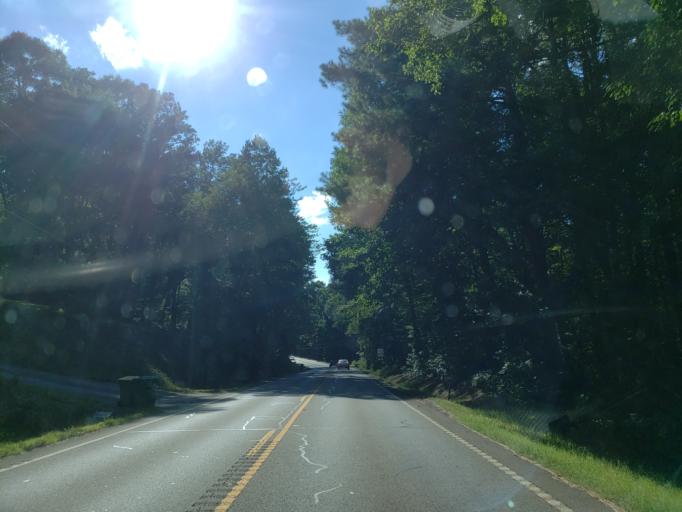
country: US
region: Georgia
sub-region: Cherokee County
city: Canton
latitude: 34.3124
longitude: -84.5396
